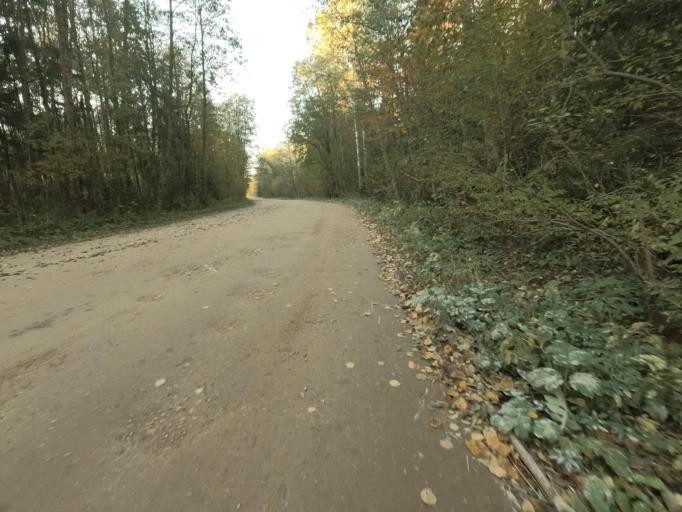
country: RU
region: Leningrad
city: Lyuban'
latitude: 59.0072
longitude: 31.0929
